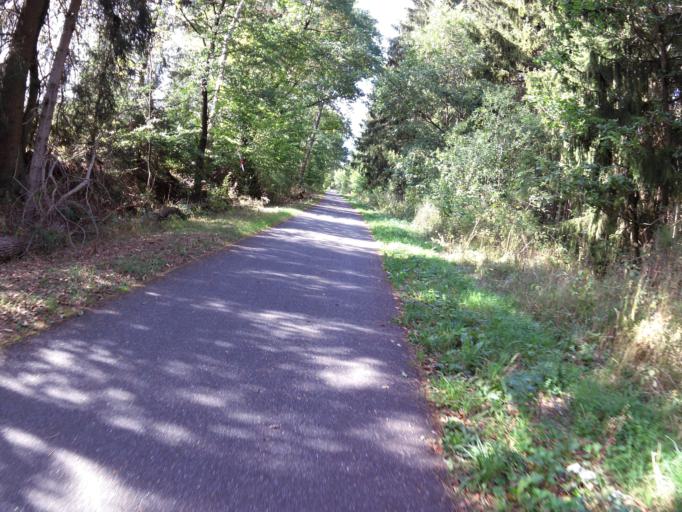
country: DE
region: Rheinland-Pfalz
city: Bleialf
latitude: 50.2160
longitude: 6.2756
